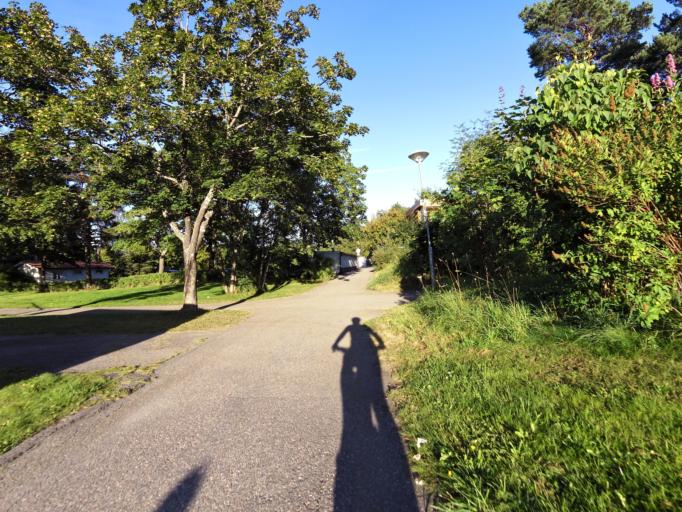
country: SE
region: Gaevleborg
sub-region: Gavle Kommun
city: Gavle
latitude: 60.6555
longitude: 17.1359
